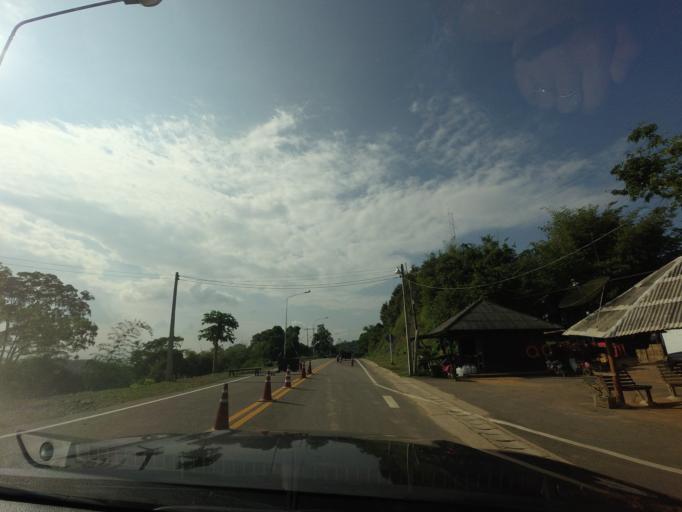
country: TH
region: Nan
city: Na Noi
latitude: 18.3700
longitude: 100.8295
